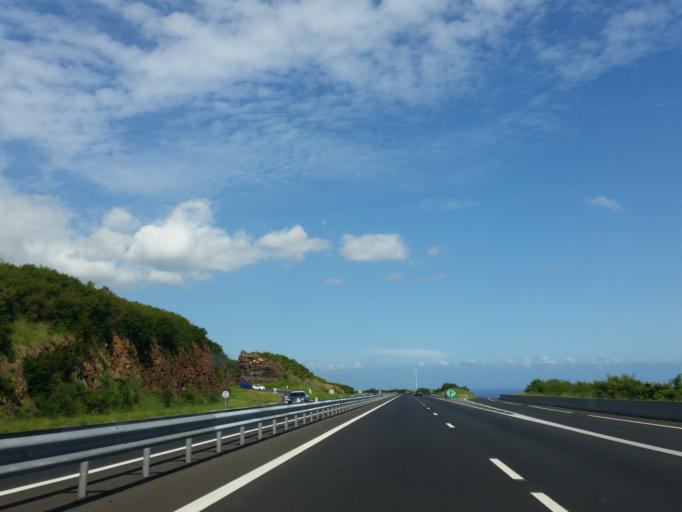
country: RE
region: Reunion
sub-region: Reunion
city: Saint-Leu
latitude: -21.1373
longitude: 55.2853
